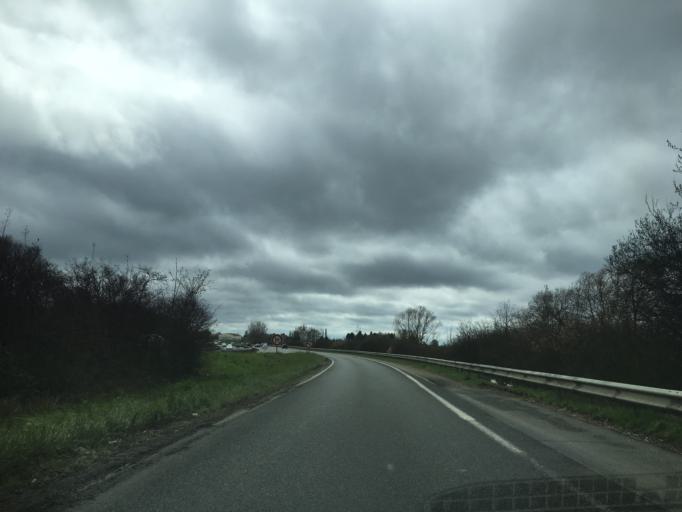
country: FR
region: Ile-de-France
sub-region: Departement de Seine-et-Marne
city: Servon
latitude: 48.7015
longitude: 2.5942
